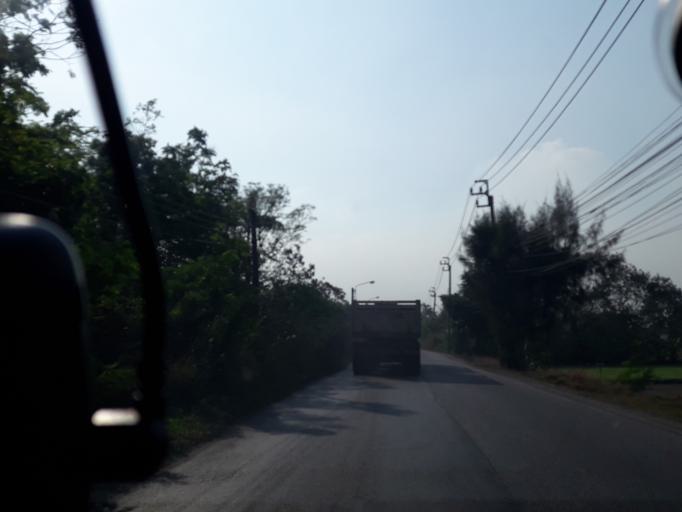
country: TH
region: Pathum Thani
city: Lam Luk Ka
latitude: 13.9130
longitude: 100.7350
